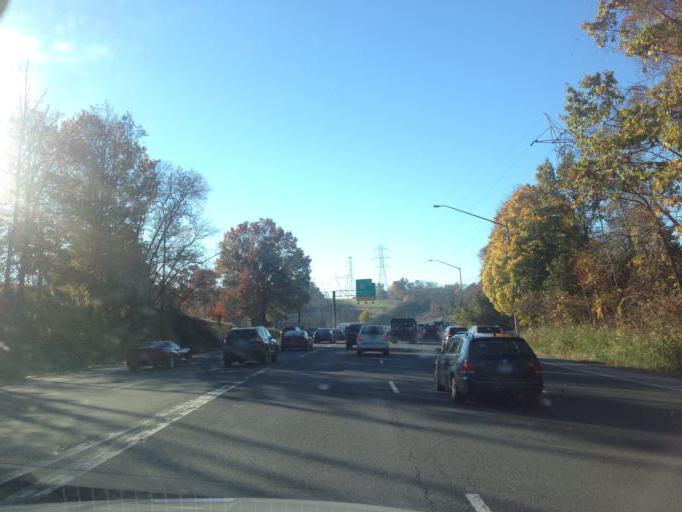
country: US
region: Maryland
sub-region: Howard County
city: Ellicott City
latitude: 39.2724
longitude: -76.8186
